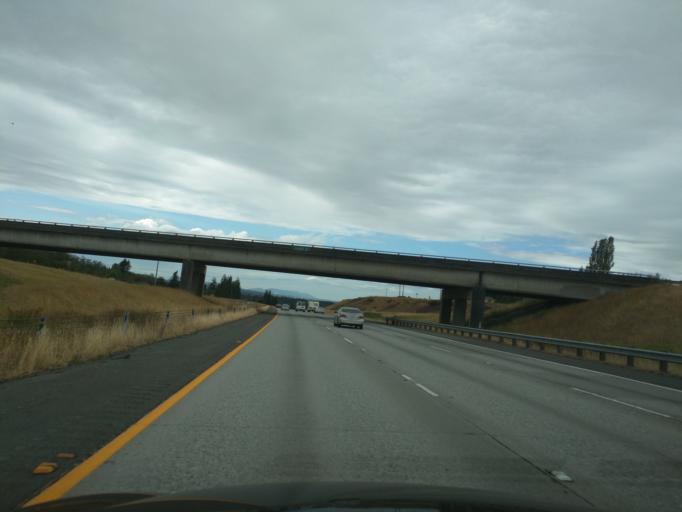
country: US
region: Washington
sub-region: Snohomish County
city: Stanwood
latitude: 48.3073
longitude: -122.3150
